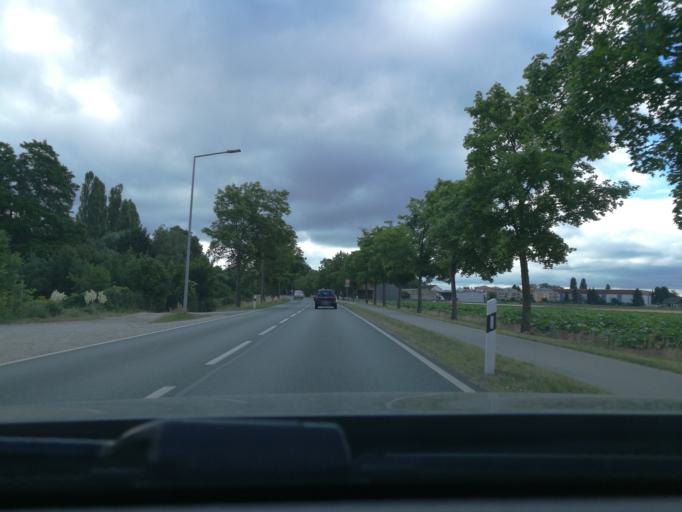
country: DE
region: Bavaria
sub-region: Regierungsbezirk Mittelfranken
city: Furth
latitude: 49.5225
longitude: 11.0176
